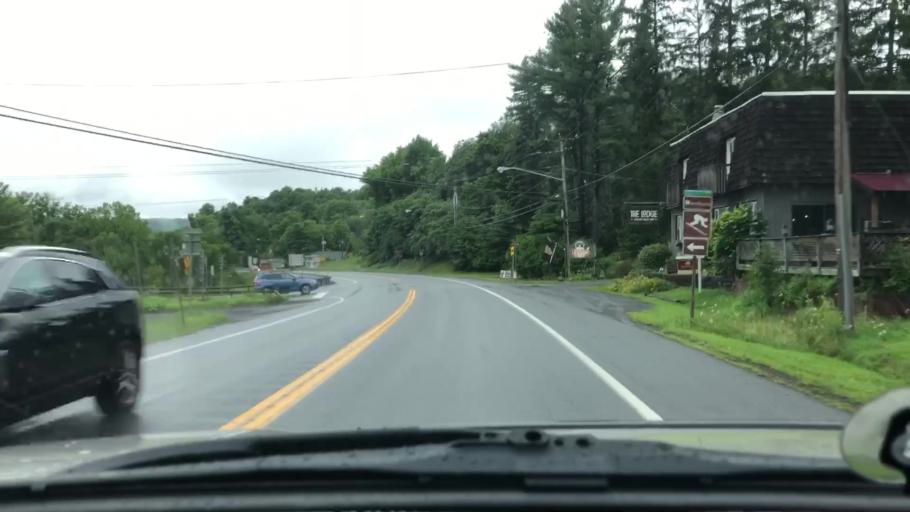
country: US
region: New York
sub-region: Greene County
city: Cairo
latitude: 42.3084
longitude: -74.2306
